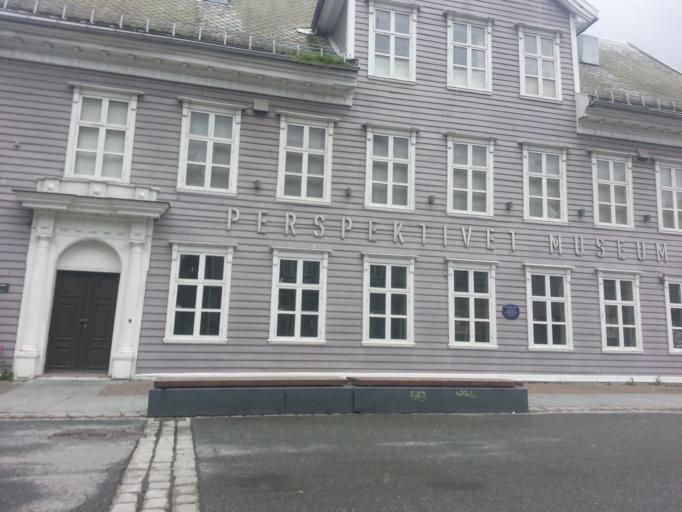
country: NO
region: Troms
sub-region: Tromso
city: Tromso
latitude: 69.6525
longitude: 18.9590
